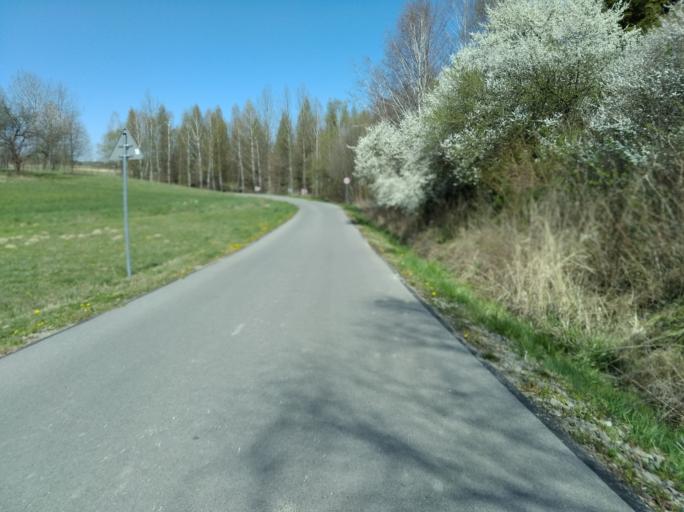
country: PL
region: Subcarpathian Voivodeship
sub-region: Powiat strzyzowski
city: Wisniowa
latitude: 49.9040
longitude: 21.6821
